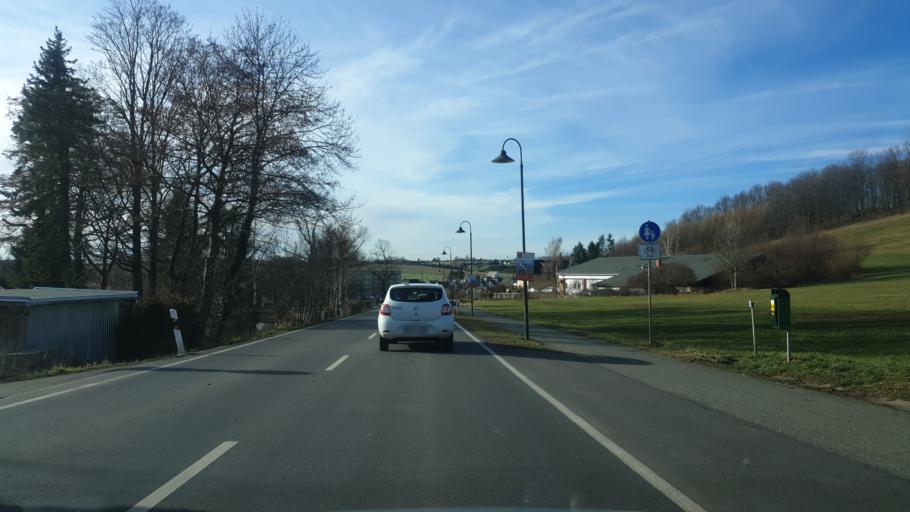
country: DE
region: Saxony
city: Wildenfels
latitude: 50.6677
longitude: 12.6169
